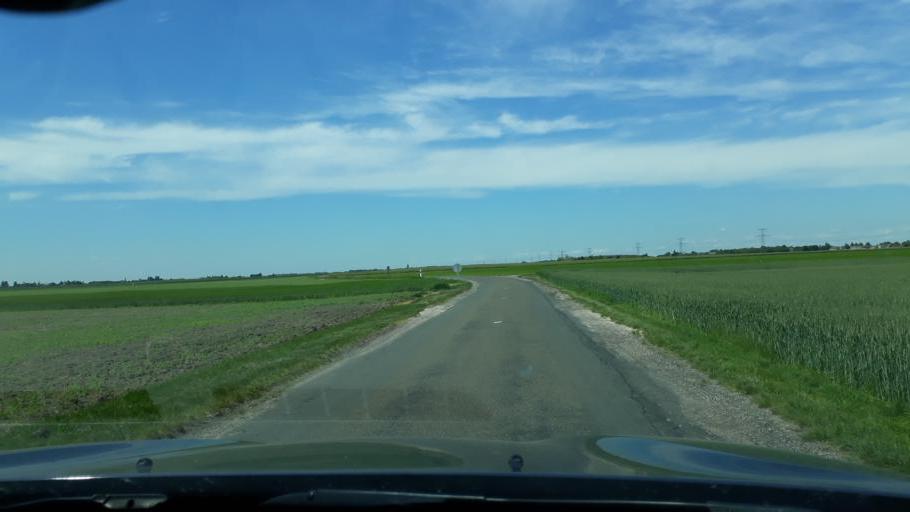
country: FR
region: Centre
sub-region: Departement du Loiret
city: Dadonville
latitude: 48.1072
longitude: 2.2381
